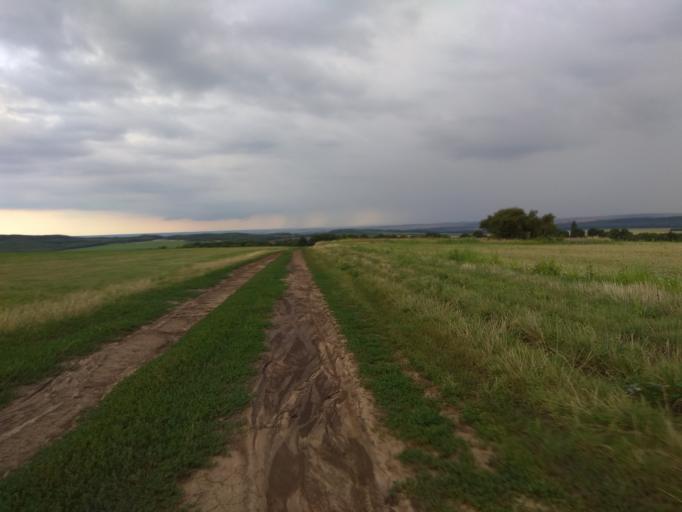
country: HU
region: Borsod-Abauj-Zemplen
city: Megyaszo
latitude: 48.1808
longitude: 21.0992
